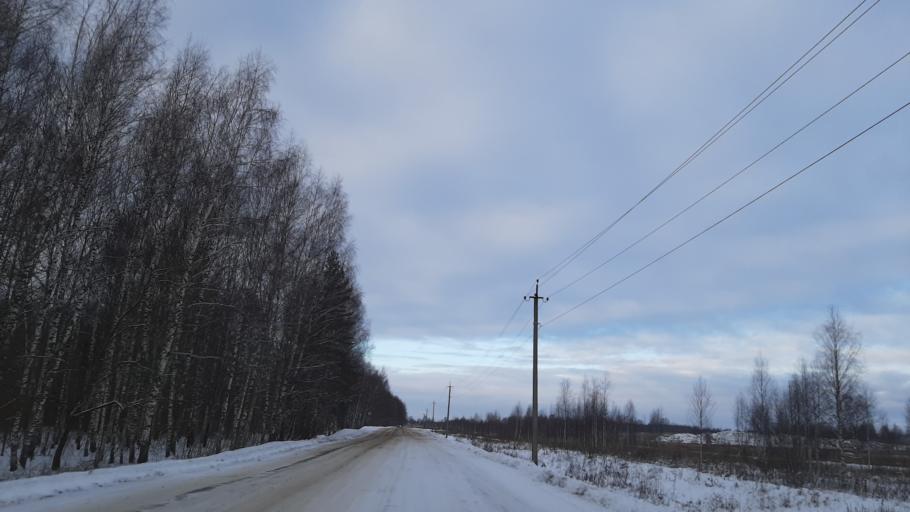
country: RU
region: Kostroma
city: Nerekhta
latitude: 57.4719
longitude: 40.6671
